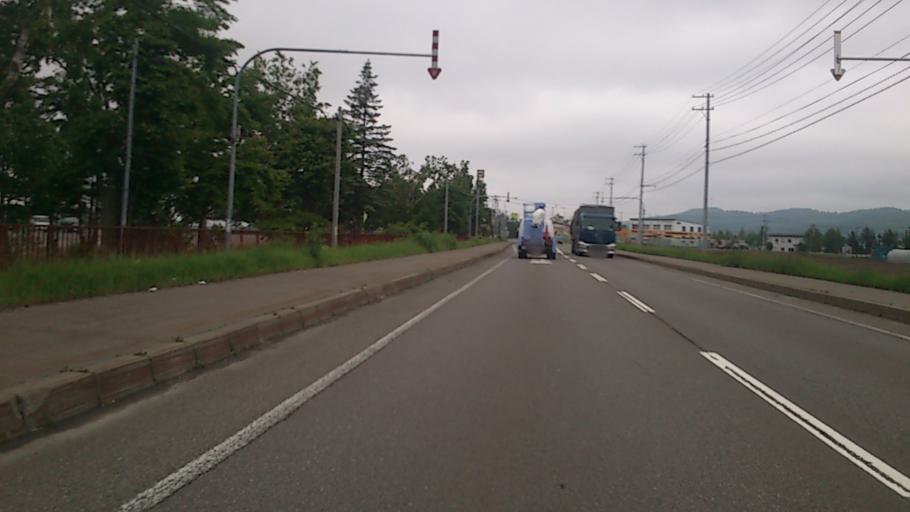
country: JP
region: Hokkaido
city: Obihiro
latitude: 42.9192
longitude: 143.3377
